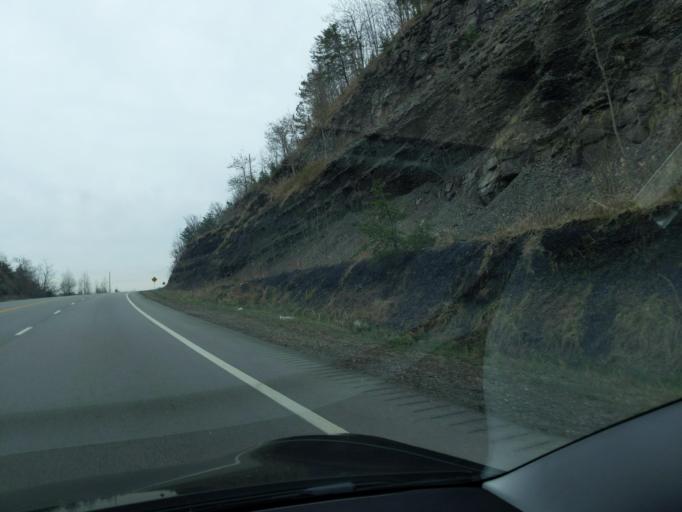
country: US
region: Kentucky
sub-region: Whitley County
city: Corbin
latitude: 36.9186
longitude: -84.1064
